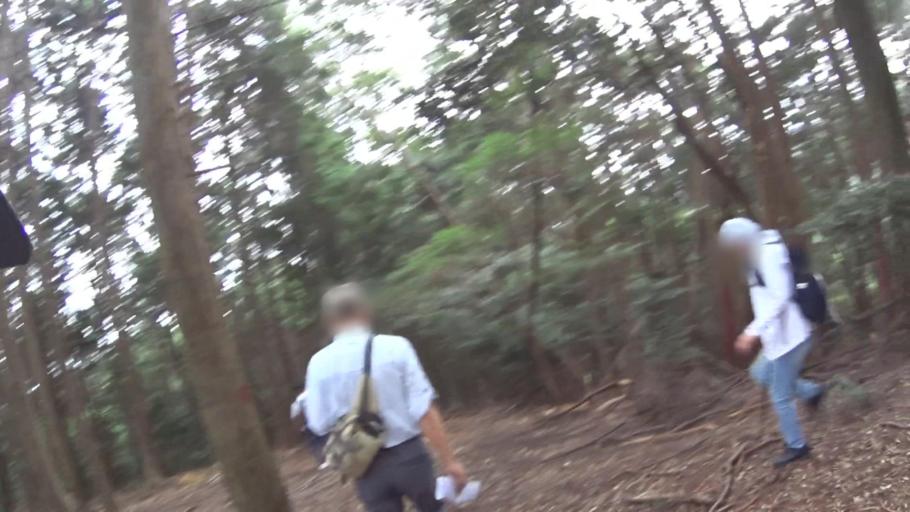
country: JP
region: Osaka
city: Kaizuka
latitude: 34.4906
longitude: 135.3232
